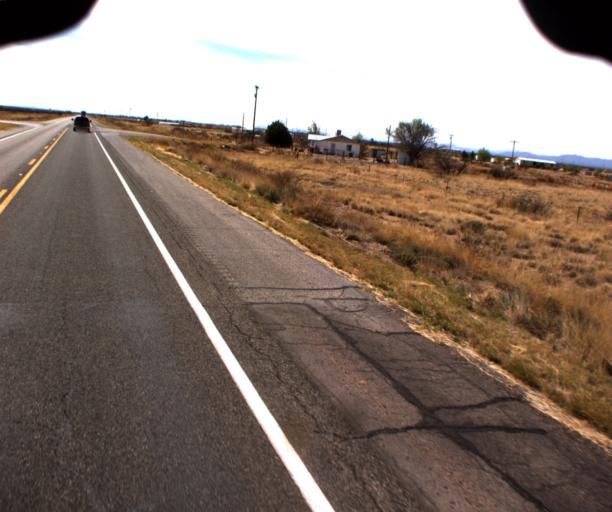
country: US
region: Arizona
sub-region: Cochise County
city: Bisbee
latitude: 31.6718
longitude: -109.6832
